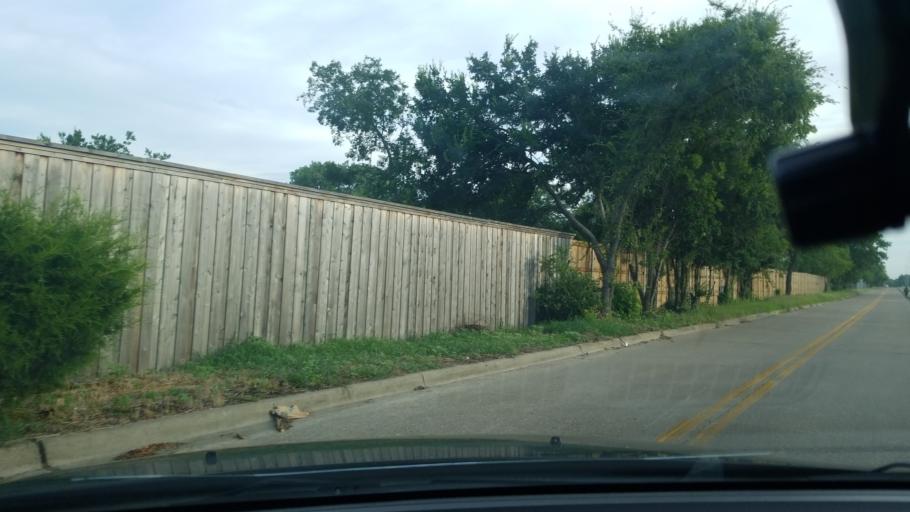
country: US
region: Texas
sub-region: Dallas County
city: Balch Springs
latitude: 32.7590
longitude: -96.6372
